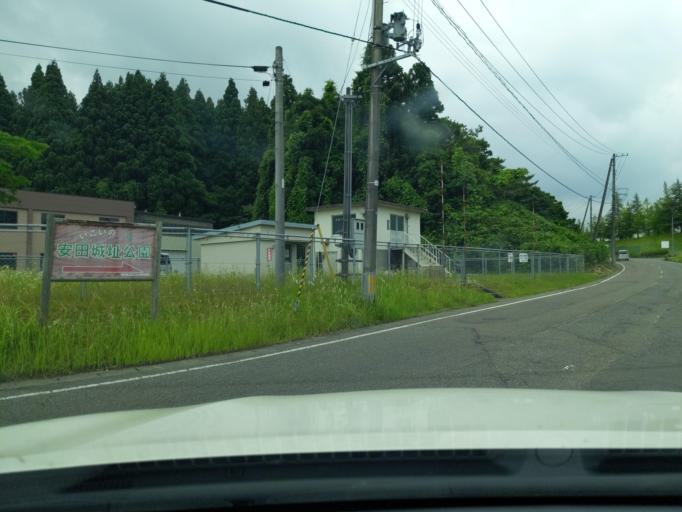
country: JP
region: Niigata
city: Kashiwazaki
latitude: 37.3461
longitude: 138.6041
